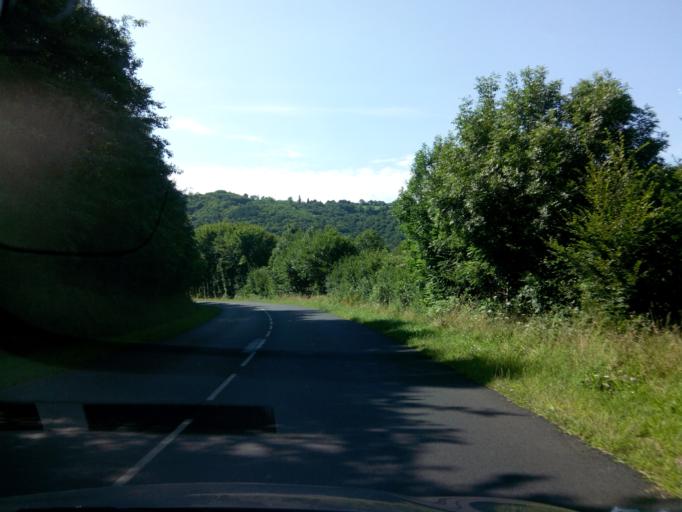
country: FR
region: Limousin
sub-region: Departement de la Correze
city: Beynat
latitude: 45.1299
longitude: 1.6820
